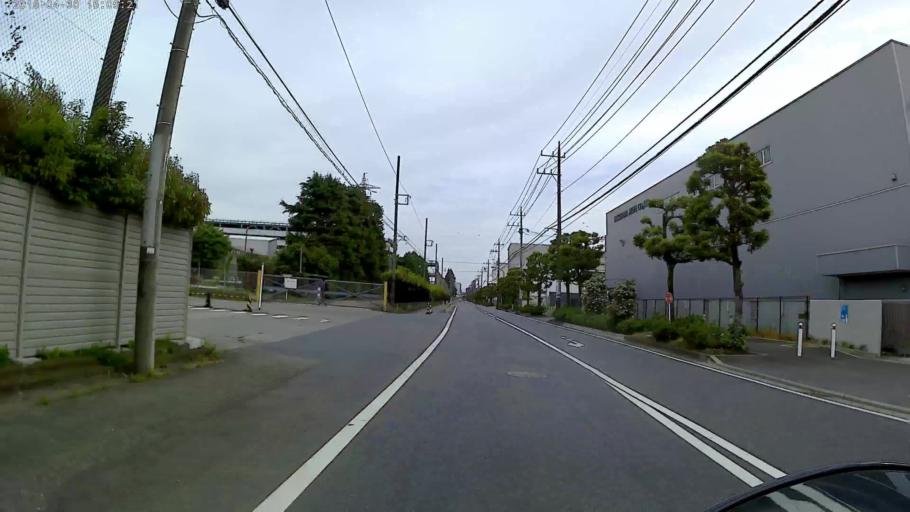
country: JP
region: Kanagawa
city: Zama
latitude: 35.5605
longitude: 139.3404
